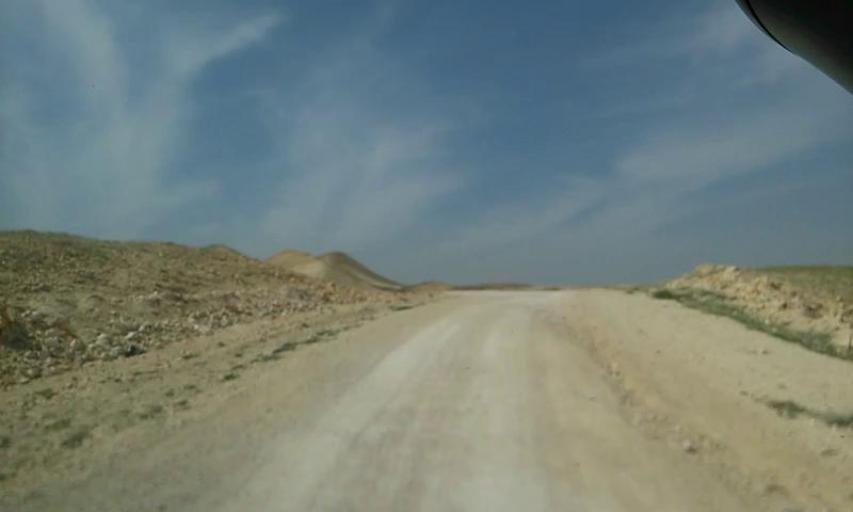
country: PS
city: `Arab ar Rashaydah
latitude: 31.4850
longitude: 35.2757
